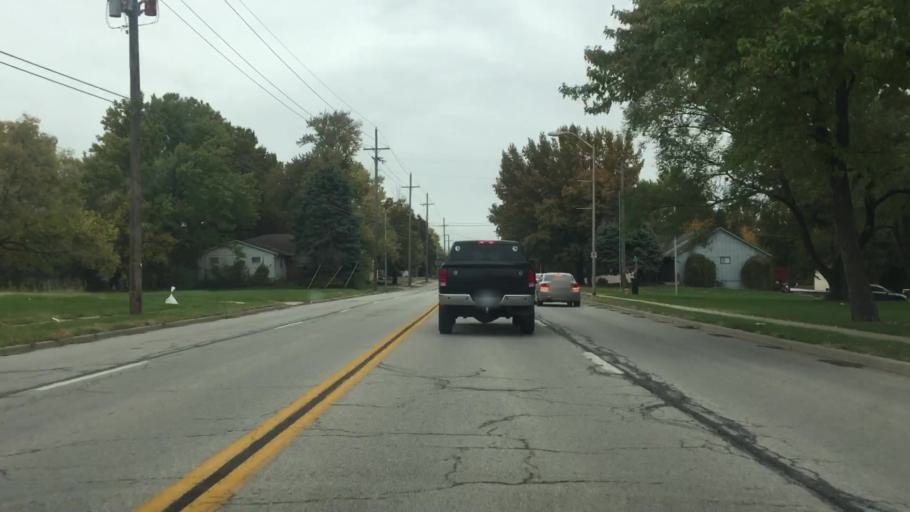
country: US
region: Kansas
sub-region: Johnson County
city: Shawnee
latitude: 39.0178
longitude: -94.7425
